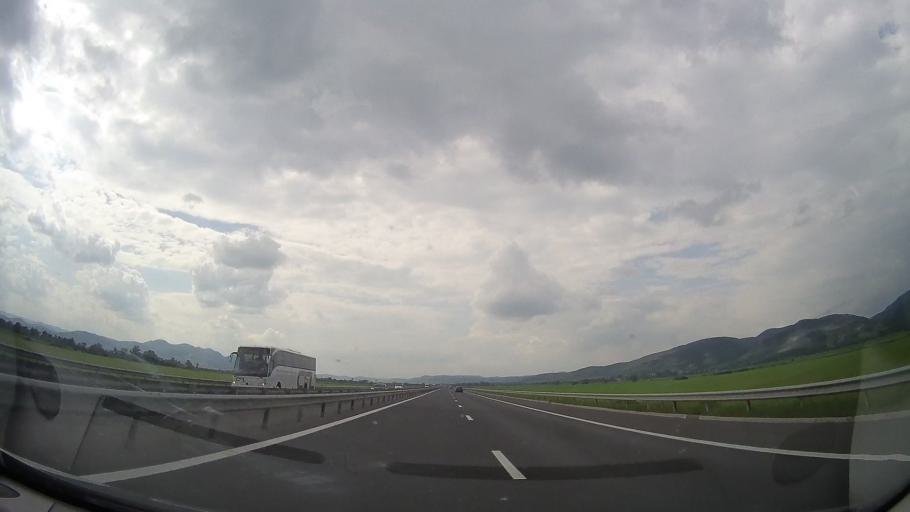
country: RO
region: Hunedoara
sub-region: Oras Simeria
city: Simeria
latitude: 45.8741
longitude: 23.0086
